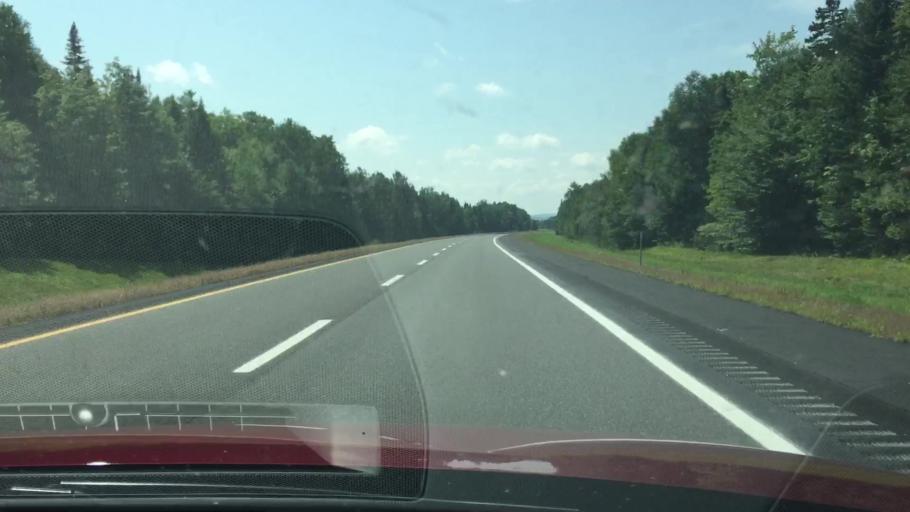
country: US
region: Maine
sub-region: Penobscot County
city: Patten
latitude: 45.9384
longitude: -68.3503
